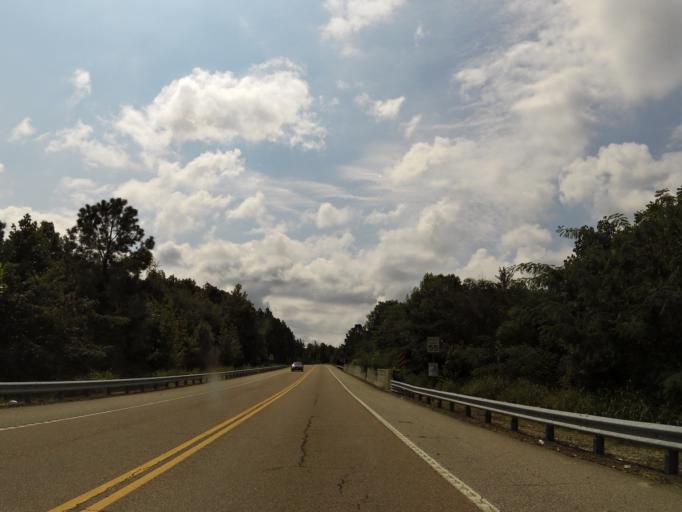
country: US
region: Tennessee
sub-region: Decatur County
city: Parsons
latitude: 35.6318
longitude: -88.0508
